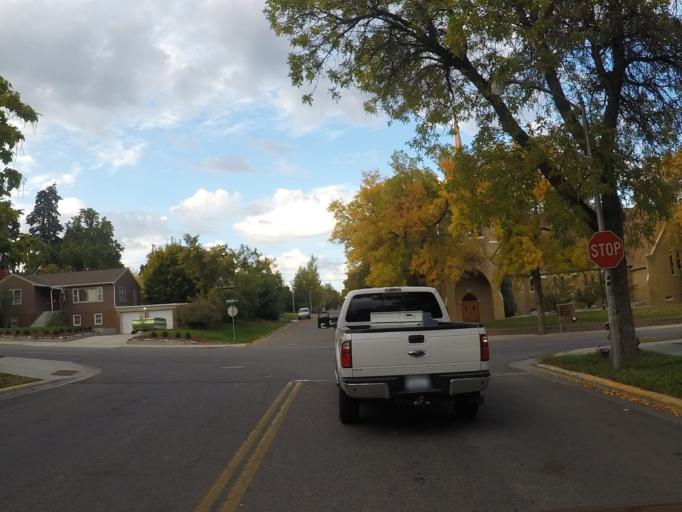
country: US
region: Montana
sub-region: Yellowstone County
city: Billings
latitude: 45.7838
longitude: -108.5306
